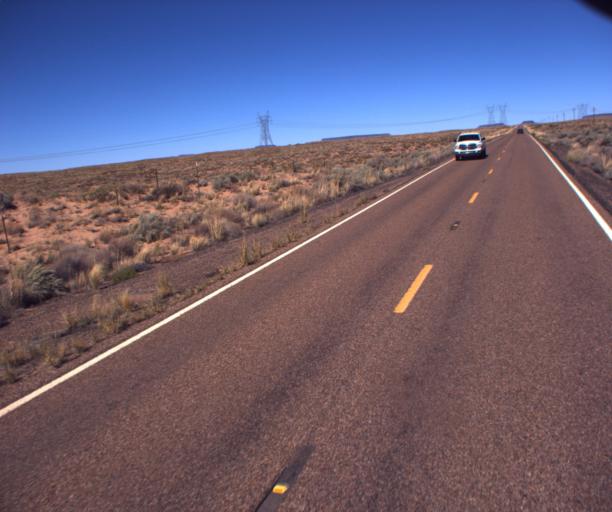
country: US
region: Arizona
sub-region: Navajo County
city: Holbrook
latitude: 35.1536
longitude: -110.0848
